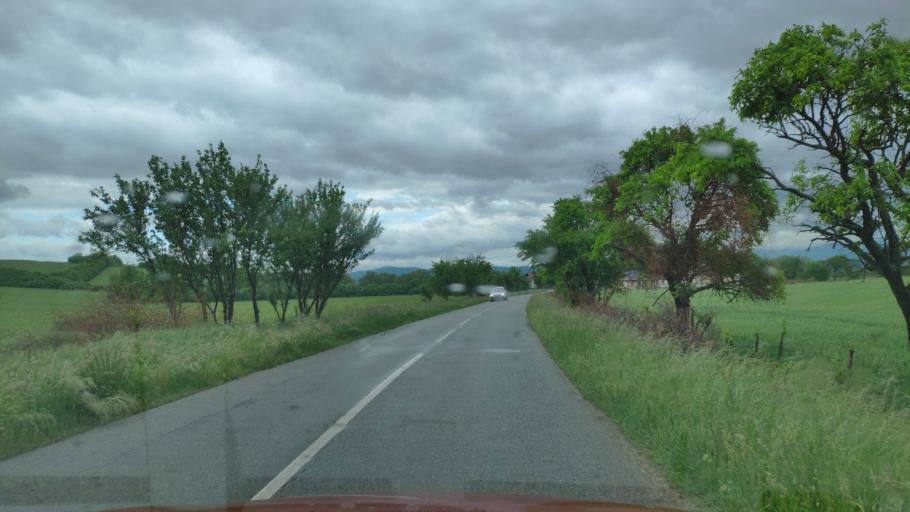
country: SK
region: Kosicky
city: Moldava nad Bodvou
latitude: 48.5405
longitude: 21.0498
